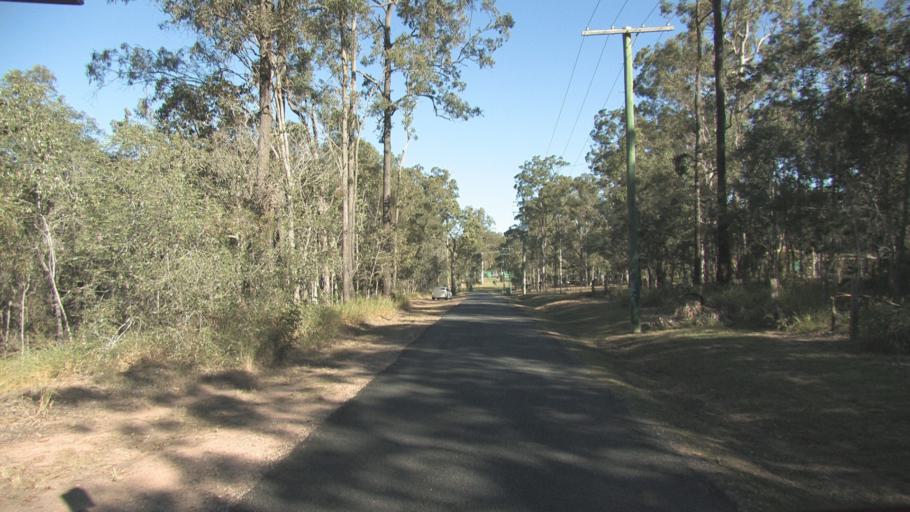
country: AU
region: Queensland
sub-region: Logan
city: Park Ridge South
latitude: -27.7217
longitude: 153.0187
